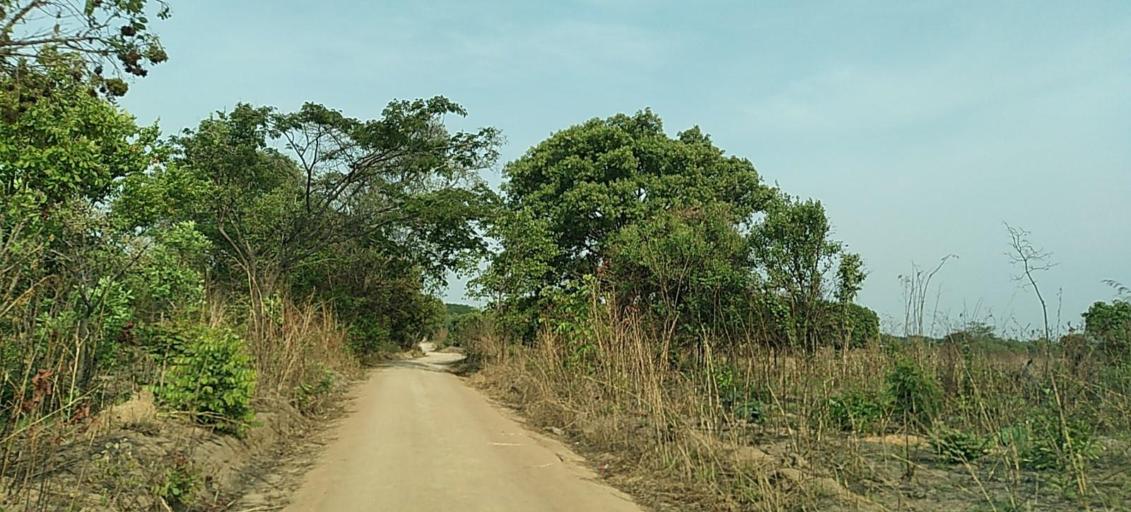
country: ZM
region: Copperbelt
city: Ndola
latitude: -13.2233
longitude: 28.6745
